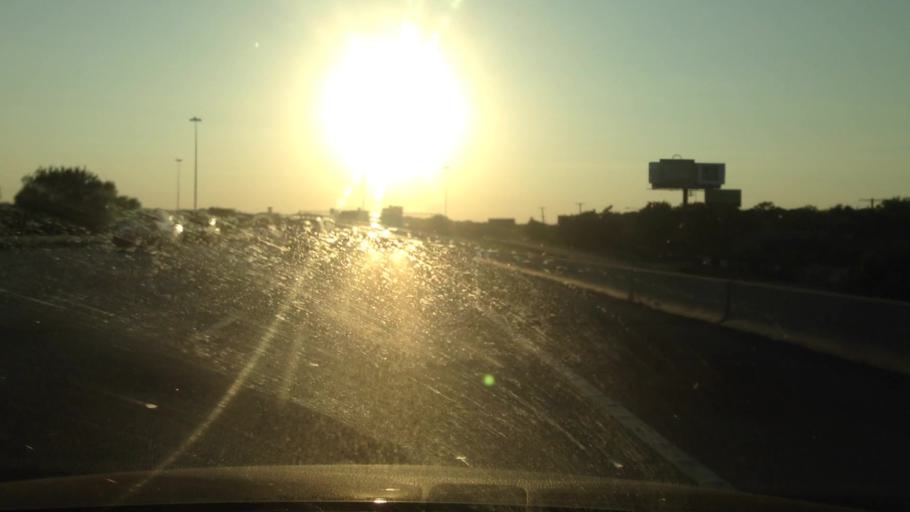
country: US
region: Texas
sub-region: Tarrant County
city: Kennedale
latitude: 32.6691
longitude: -97.2322
